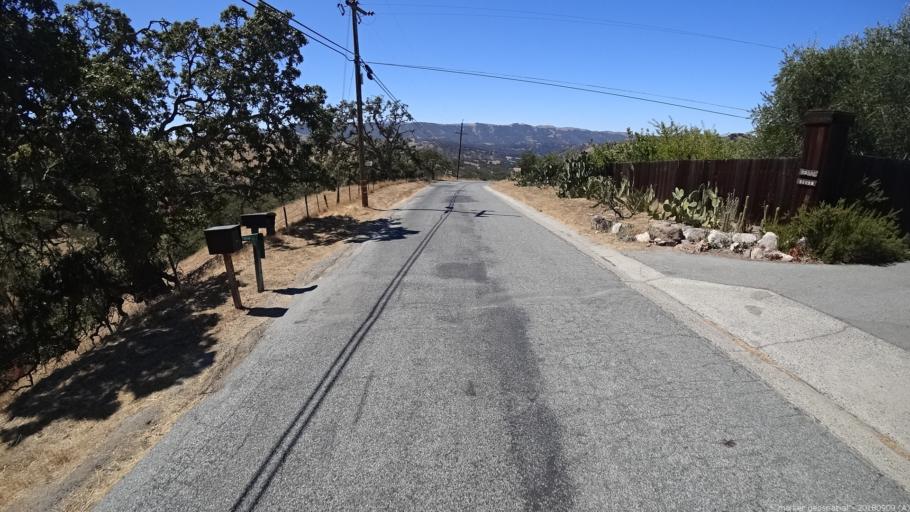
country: US
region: California
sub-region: Monterey County
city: Carmel Valley Village
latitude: 36.5403
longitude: -121.6554
